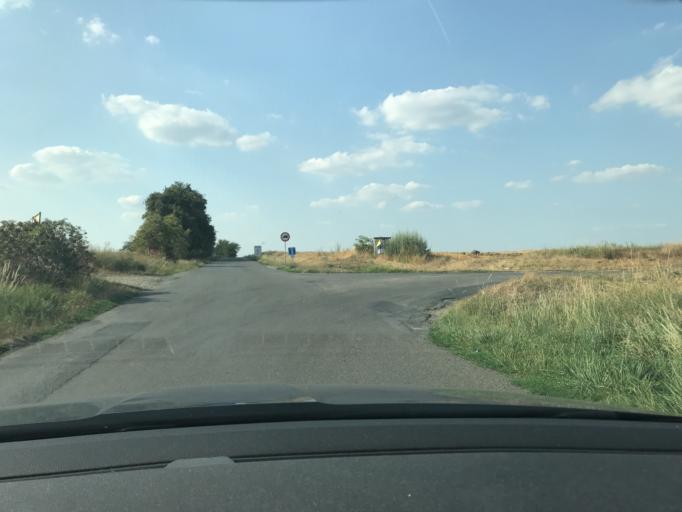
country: CZ
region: Central Bohemia
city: Kralupy nad Vltavou
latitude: 50.2264
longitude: 14.3212
